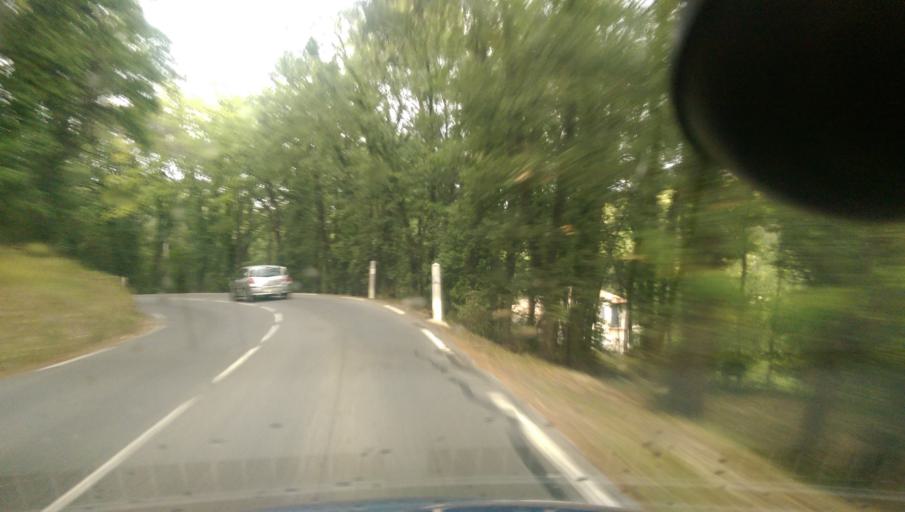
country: FR
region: Provence-Alpes-Cote d'Azur
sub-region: Departement des Alpes-Maritimes
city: Chateauneuf-Grasse
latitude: 43.6560
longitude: 7.0038
